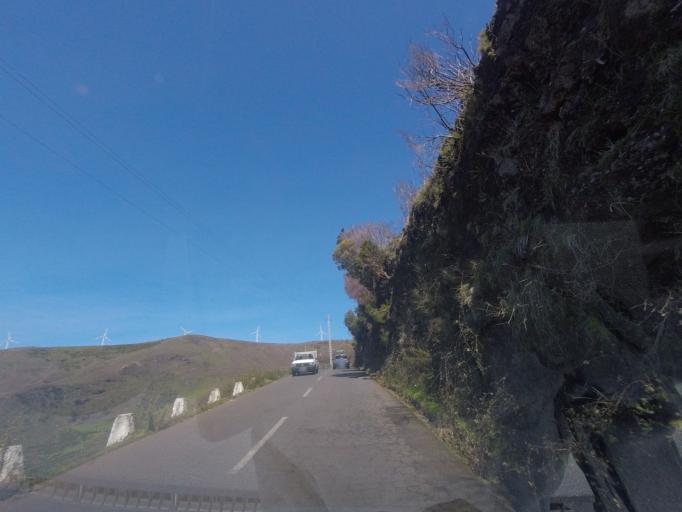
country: PT
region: Madeira
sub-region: Calheta
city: Arco da Calheta
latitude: 32.7357
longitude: -17.1042
